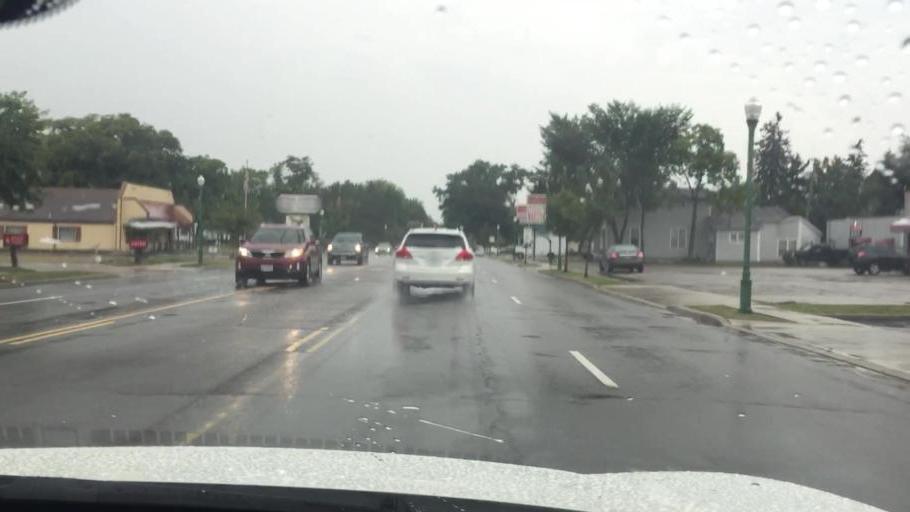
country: US
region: Ohio
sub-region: Champaign County
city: Urbana
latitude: 40.1073
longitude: -83.7387
